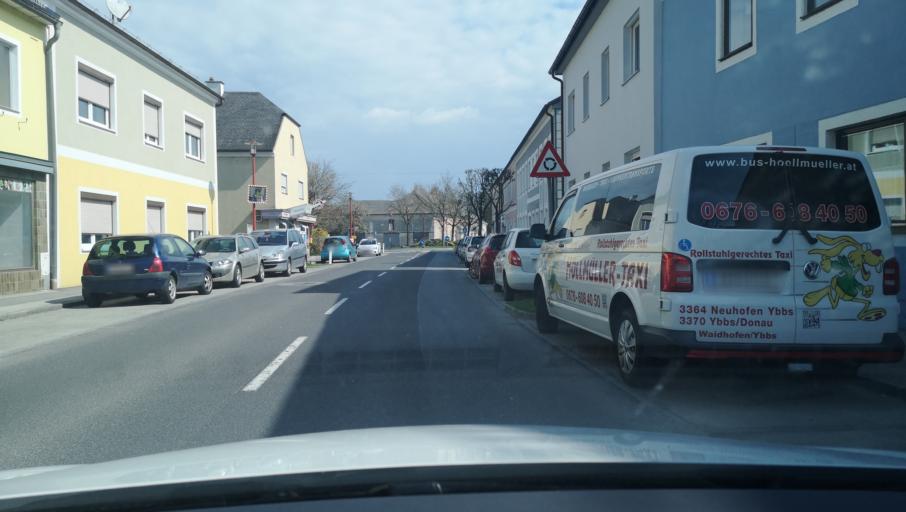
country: AT
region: Lower Austria
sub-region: Politischer Bezirk Amstetten
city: Zeillern
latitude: 48.0967
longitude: 14.8004
